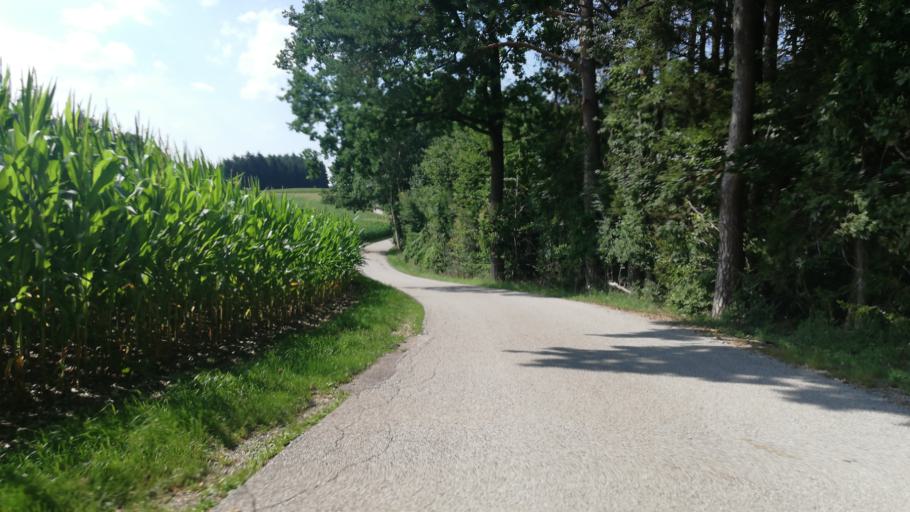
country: AT
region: Upper Austria
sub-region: Wels-Land
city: Pennewang
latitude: 48.1609
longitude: 13.8624
